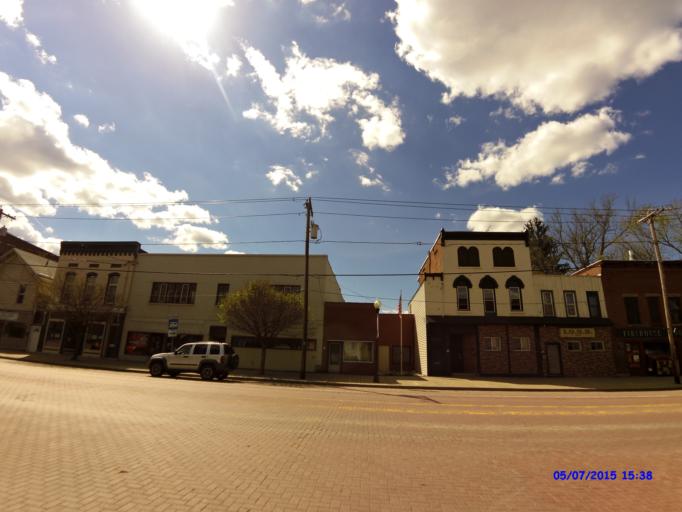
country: US
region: New York
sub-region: Cattaraugus County
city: Franklinville
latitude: 42.3377
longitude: -78.4576
